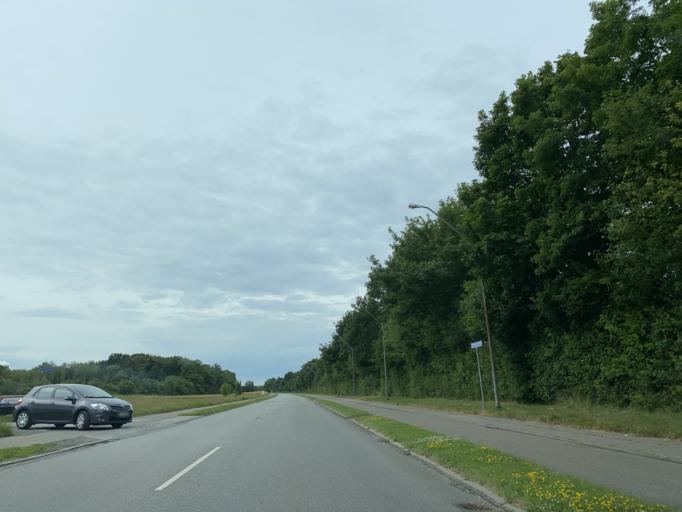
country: DK
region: South Denmark
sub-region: Sonderborg Kommune
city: Sonderborg
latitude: 54.9140
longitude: 9.8281
